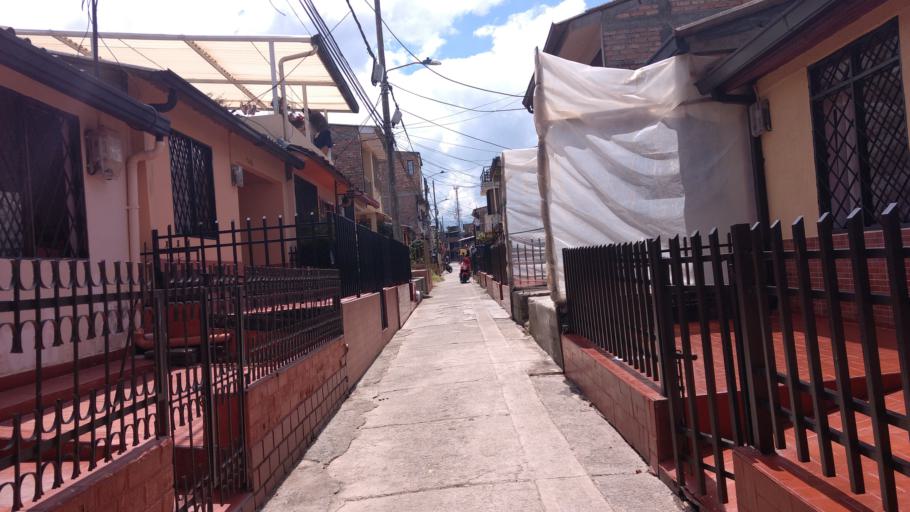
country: CO
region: Cauca
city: Popayan
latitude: 2.4764
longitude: -76.5601
